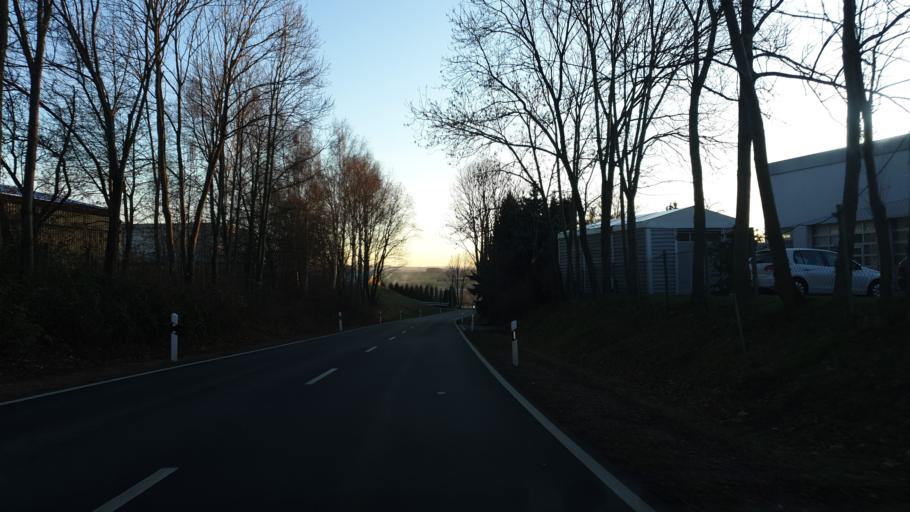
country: DE
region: Saxony
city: Kirchberg
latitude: 50.8048
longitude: 12.7601
